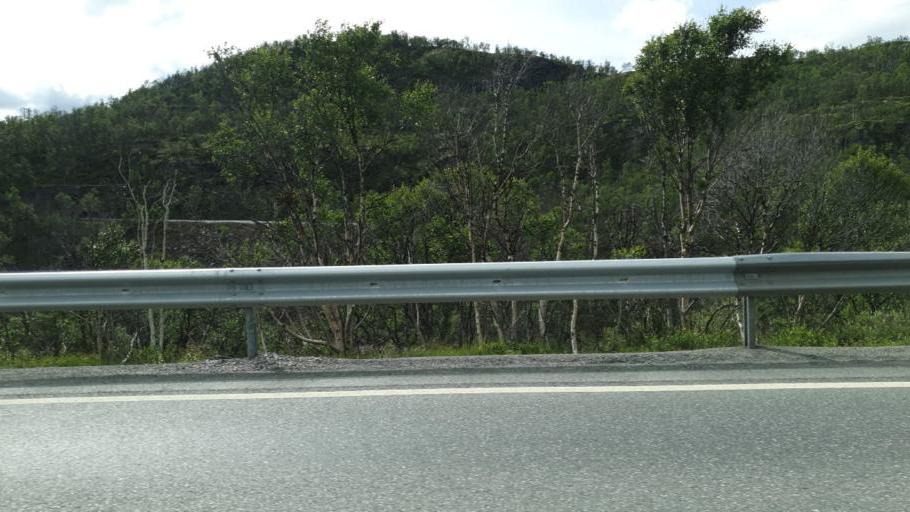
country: NO
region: Sor-Trondelag
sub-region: Oppdal
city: Oppdal
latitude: 62.2947
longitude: 9.5945
